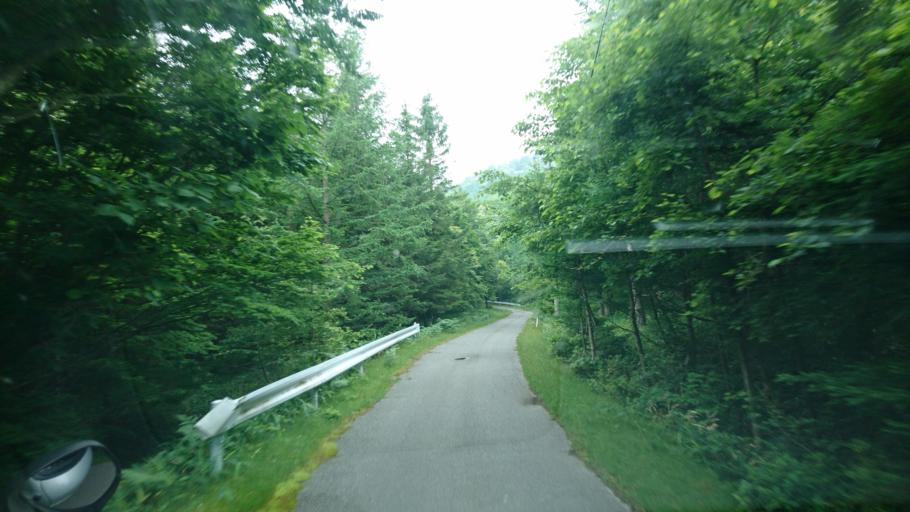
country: JP
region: Iwate
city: Ofunato
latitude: 39.1687
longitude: 141.7551
